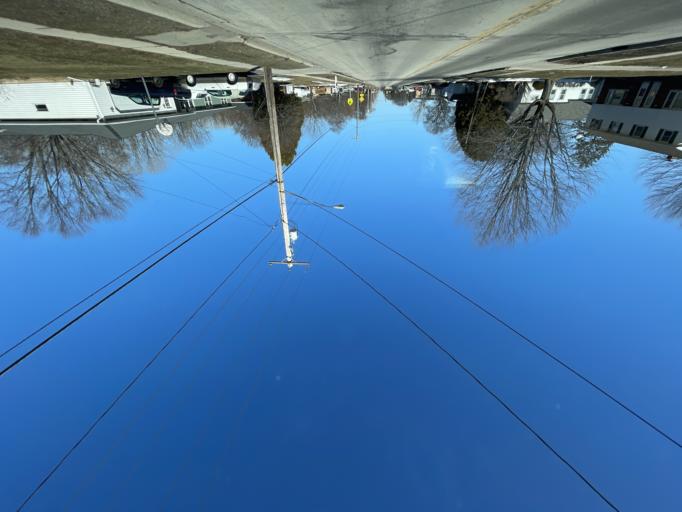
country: US
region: Wisconsin
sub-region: Brown County
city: Howard
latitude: 44.5706
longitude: -88.0847
